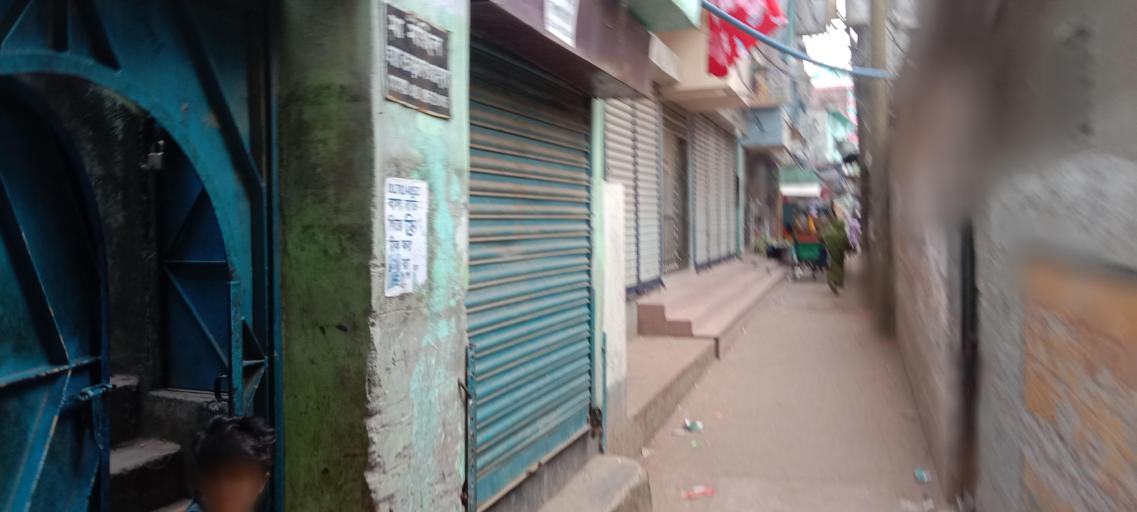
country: BD
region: Dhaka
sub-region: Dhaka
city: Dhaka
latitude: 23.6992
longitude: 90.4110
